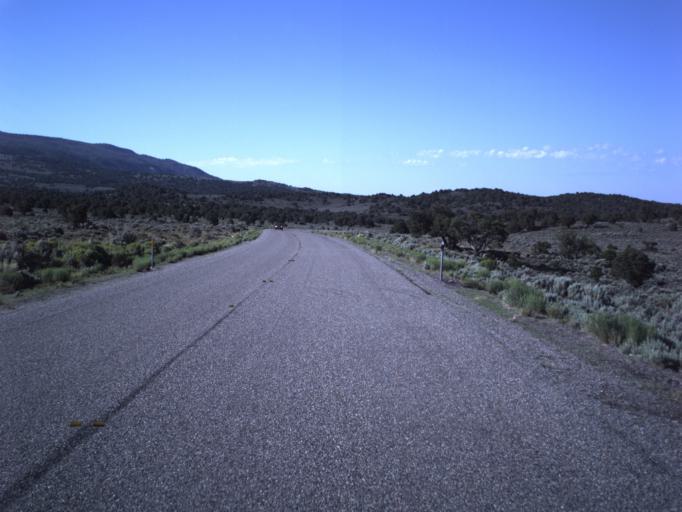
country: US
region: Utah
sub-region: Wayne County
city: Loa
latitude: 38.4975
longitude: -111.5349
